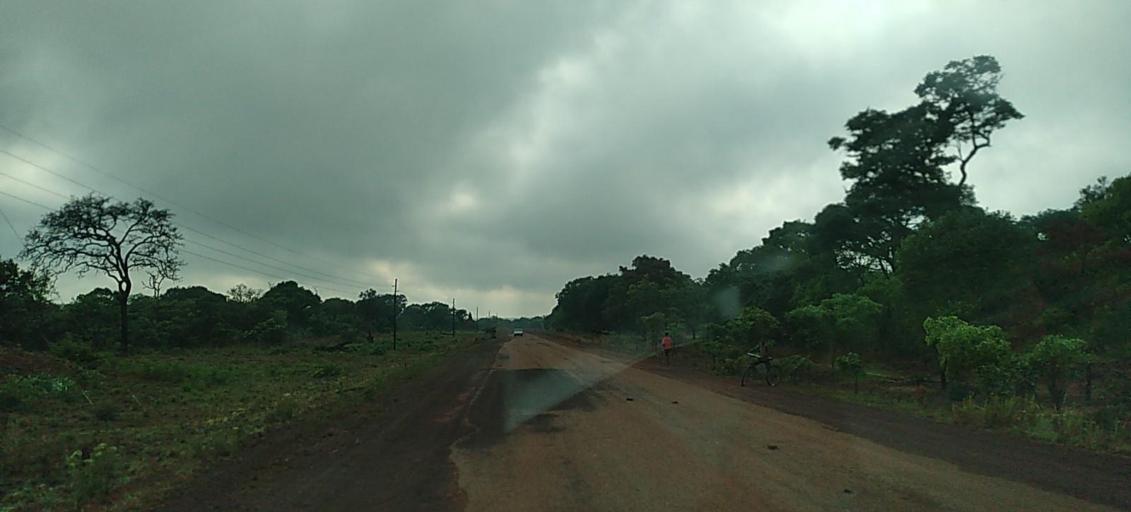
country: ZM
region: North-Western
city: Mwinilunga
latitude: -11.7251
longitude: 24.5710
